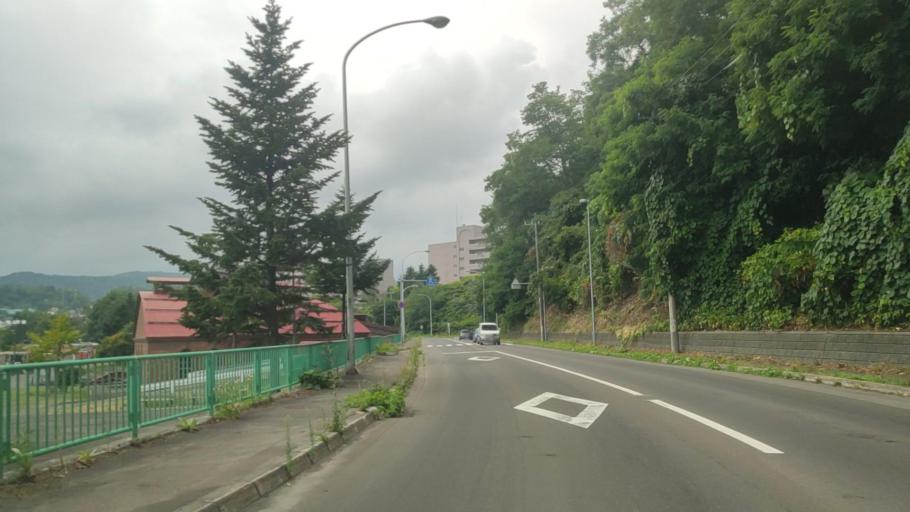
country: JP
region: Hokkaido
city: Otaru
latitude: 43.2124
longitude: 141.0012
